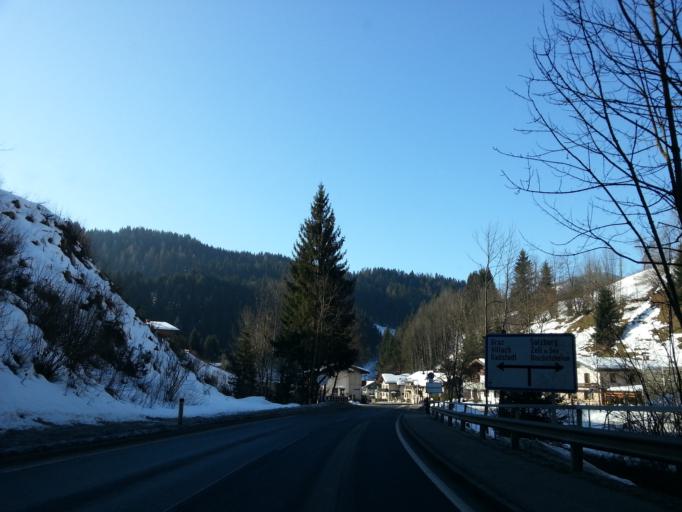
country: AT
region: Salzburg
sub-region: Politischer Bezirk Sankt Johann im Pongau
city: Huttau
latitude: 47.4246
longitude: 13.3468
